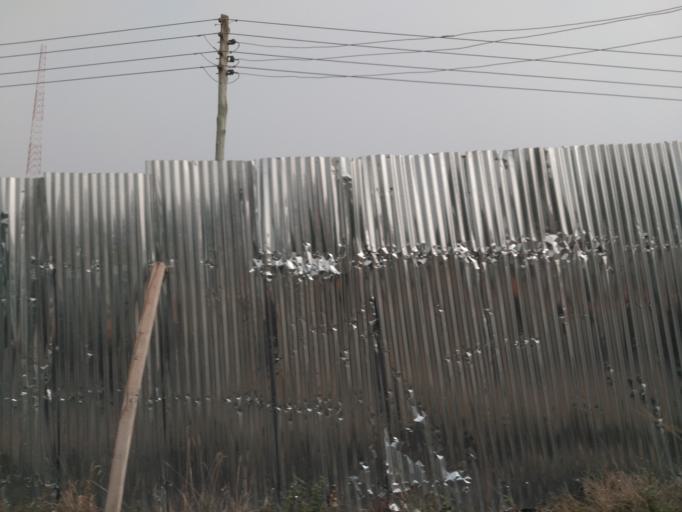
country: GH
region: Ashanti
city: Kumasi
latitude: 6.6543
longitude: -1.6312
